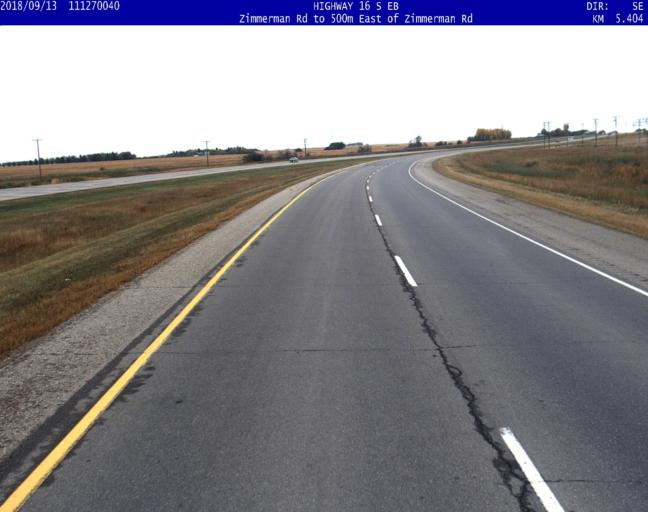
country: CA
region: Saskatchewan
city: Saskatoon
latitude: 52.0850
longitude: -106.5200
